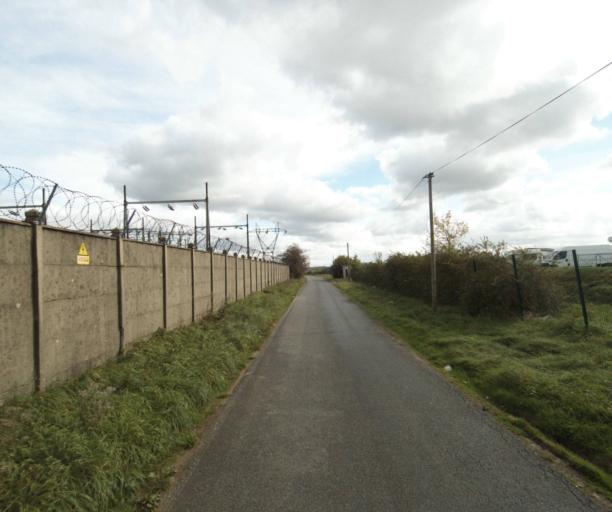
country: FR
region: Nord-Pas-de-Calais
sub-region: Departement du Nord
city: Armentieres
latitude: 50.6806
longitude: 2.8975
